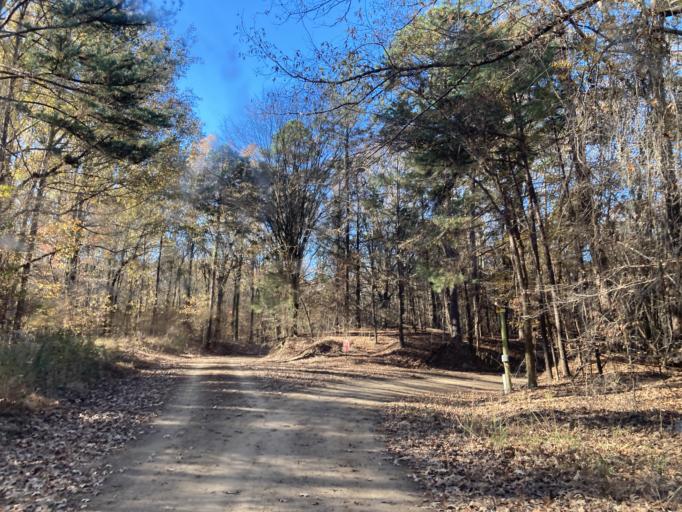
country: US
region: Mississippi
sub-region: Madison County
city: Kearney Park
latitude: 32.6711
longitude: -90.4491
